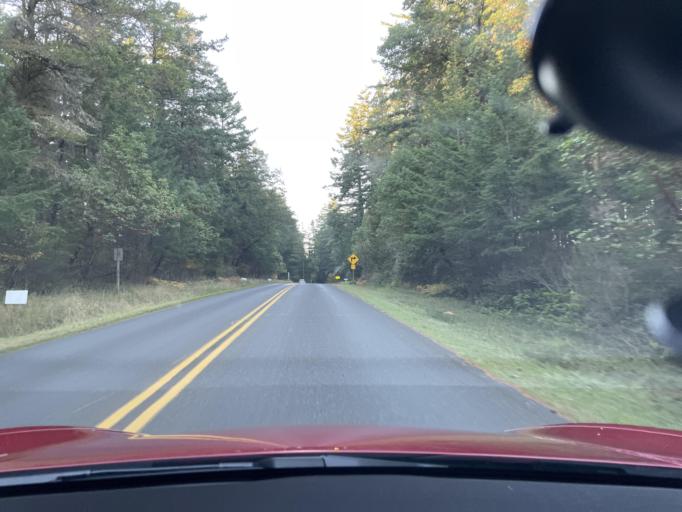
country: US
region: Washington
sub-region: San Juan County
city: Friday Harbor
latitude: 48.5637
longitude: -123.1648
